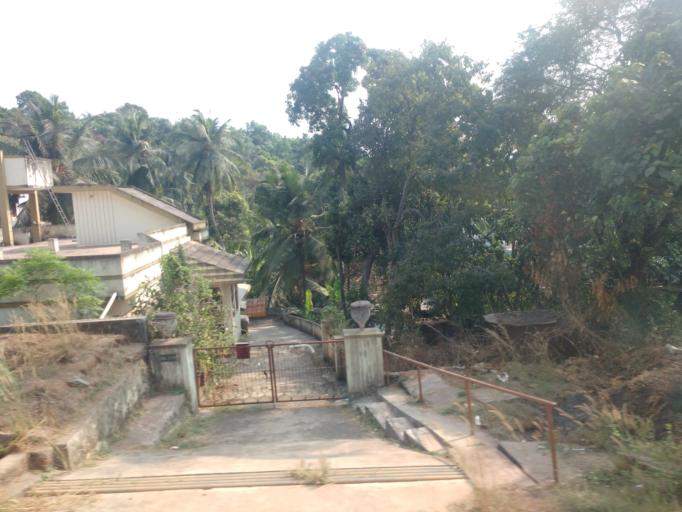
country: IN
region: Karnataka
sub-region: Dakshina Kannada
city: Mangalore
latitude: 12.8701
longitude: 74.8786
